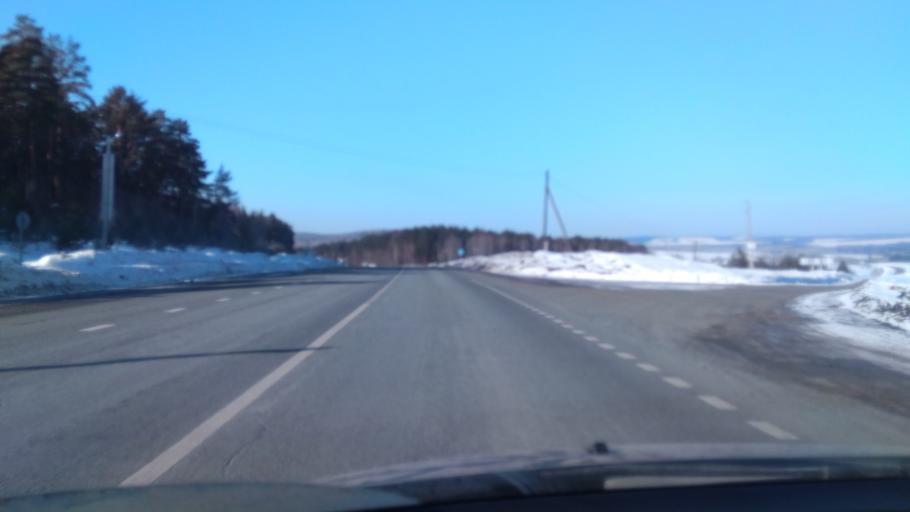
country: RU
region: Sverdlovsk
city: Bisert'
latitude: 56.8333
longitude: 58.7954
